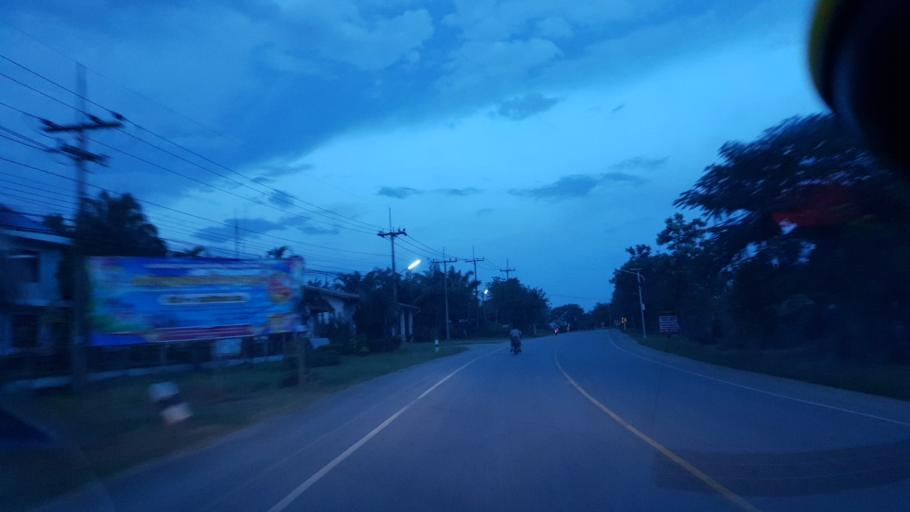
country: TH
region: Chiang Rai
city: Wiang Chiang Rung
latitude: 19.9946
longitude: 100.0366
